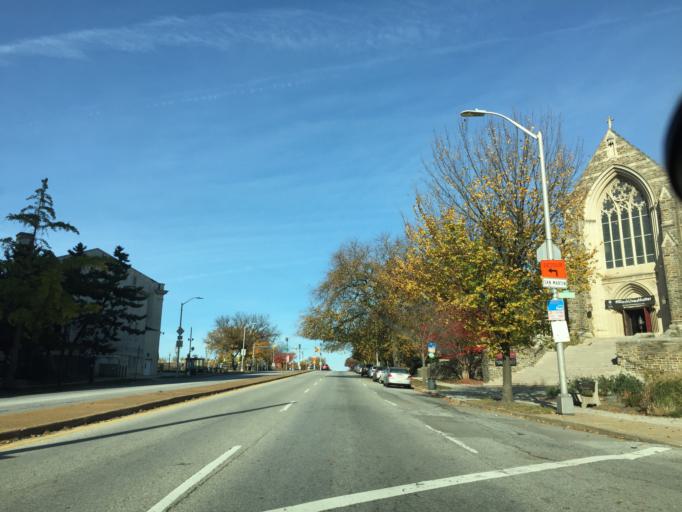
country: US
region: Maryland
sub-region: City of Baltimore
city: Baltimore
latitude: 39.3317
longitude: -76.6163
